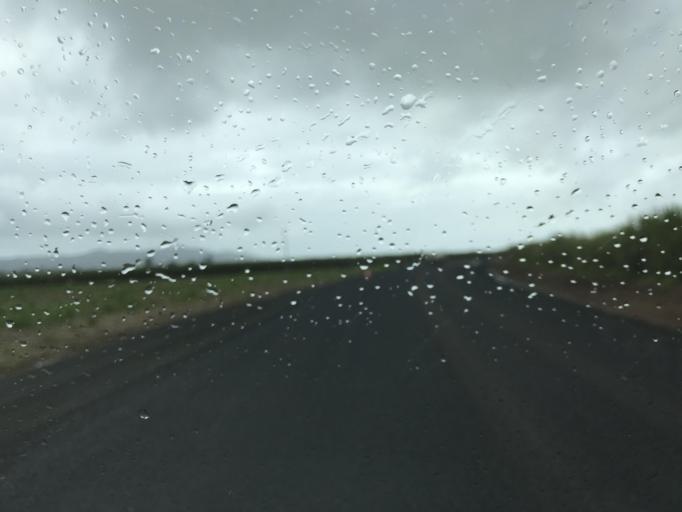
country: AU
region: Queensland
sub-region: Cassowary Coast
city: Innisfail
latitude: -17.5001
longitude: 145.9861
